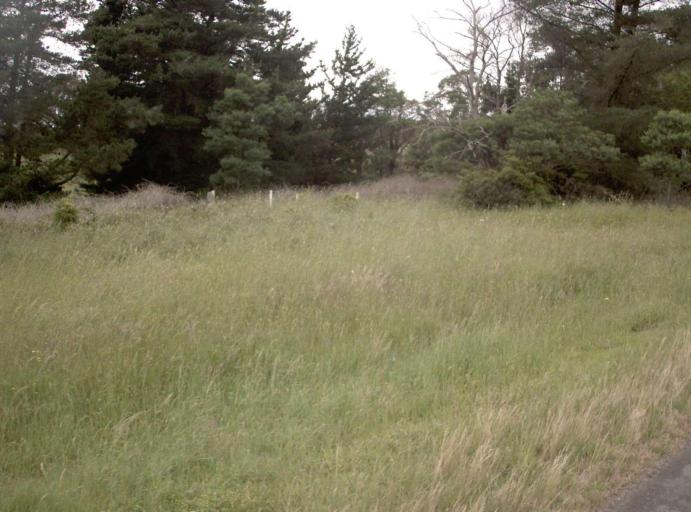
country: AU
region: Victoria
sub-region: Baw Baw
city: Warragul
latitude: -38.4581
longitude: 145.9304
